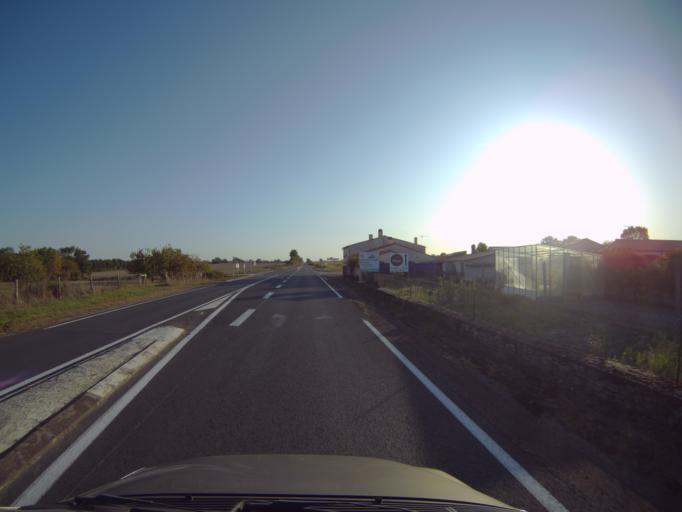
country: FR
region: Pays de la Loire
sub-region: Departement de la Vendee
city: La Bernardiere
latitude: 47.0409
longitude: -1.2528
